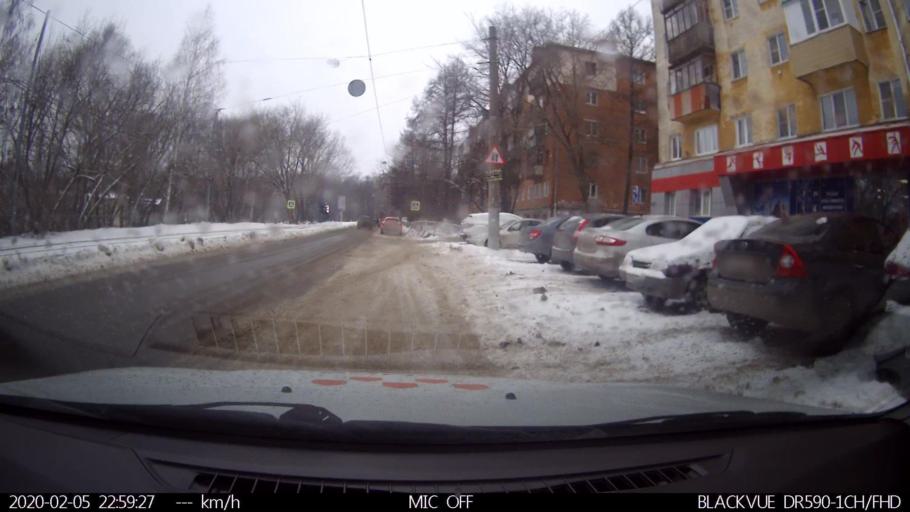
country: RU
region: Penza
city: Bogoslovka
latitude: 53.2065
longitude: 44.8645
